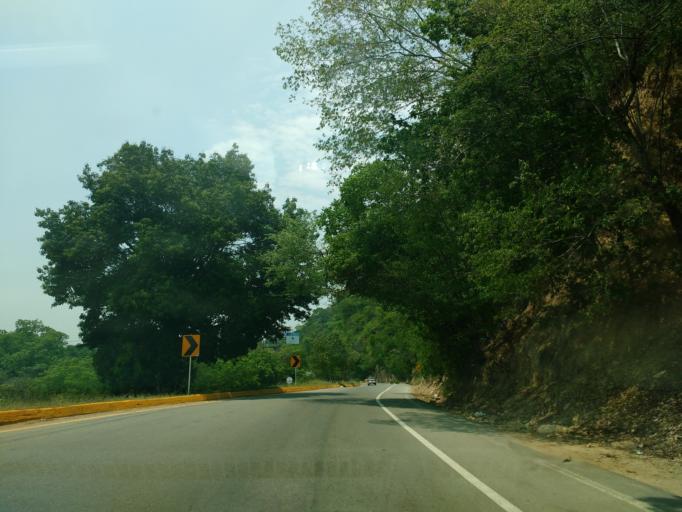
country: CO
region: Cundinamarca
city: Ricaurte
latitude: 4.2456
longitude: -74.7441
